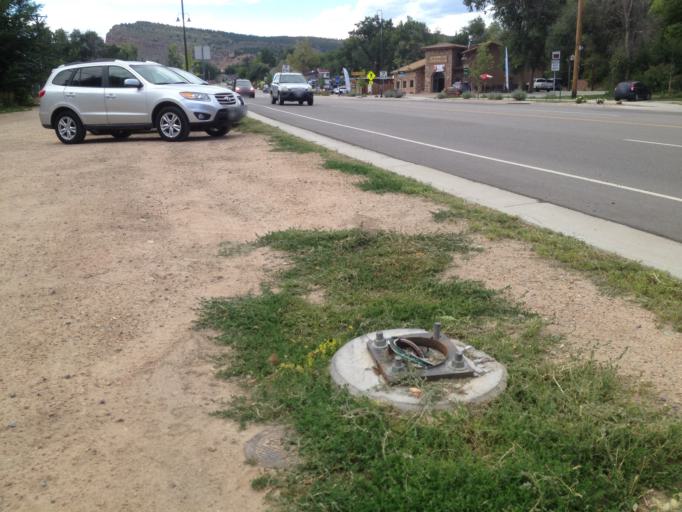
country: US
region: Colorado
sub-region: Boulder County
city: Lyons
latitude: 40.2211
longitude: -105.2636
